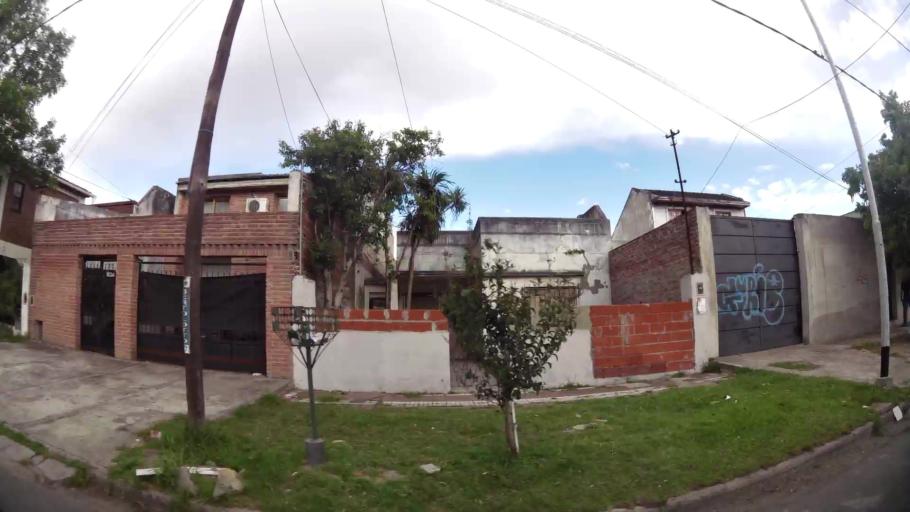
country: AR
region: Buenos Aires
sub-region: Partido de Lanus
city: Lanus
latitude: -34.6918
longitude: -58.3674
